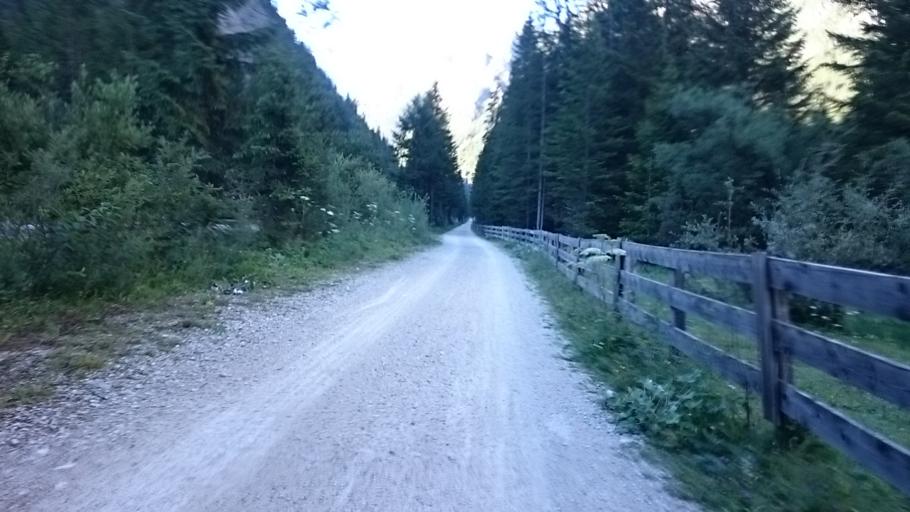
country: IT
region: Trentino-Alto Adige
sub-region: Bolzano
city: Dobbiaco
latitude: 46.6792
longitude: 12.2231
